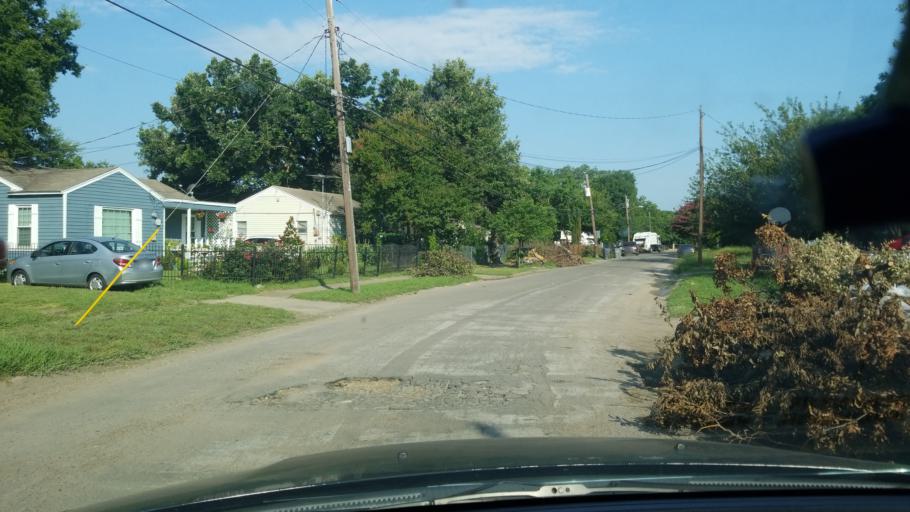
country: US
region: Texas
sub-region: Dallas County
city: Balch Springs
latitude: 32.7228
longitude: -96.6909
